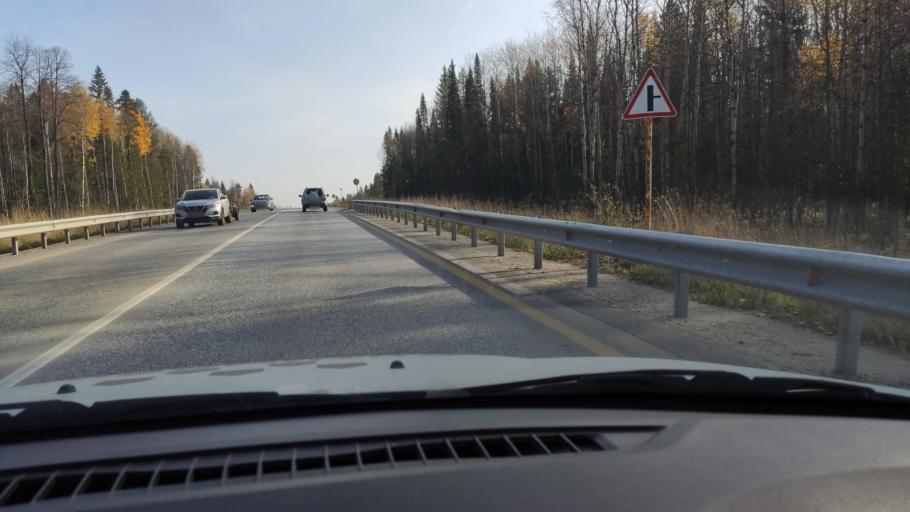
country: RU
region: Perm
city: Novyye Lyady
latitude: 58.0494
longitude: 56.5563
